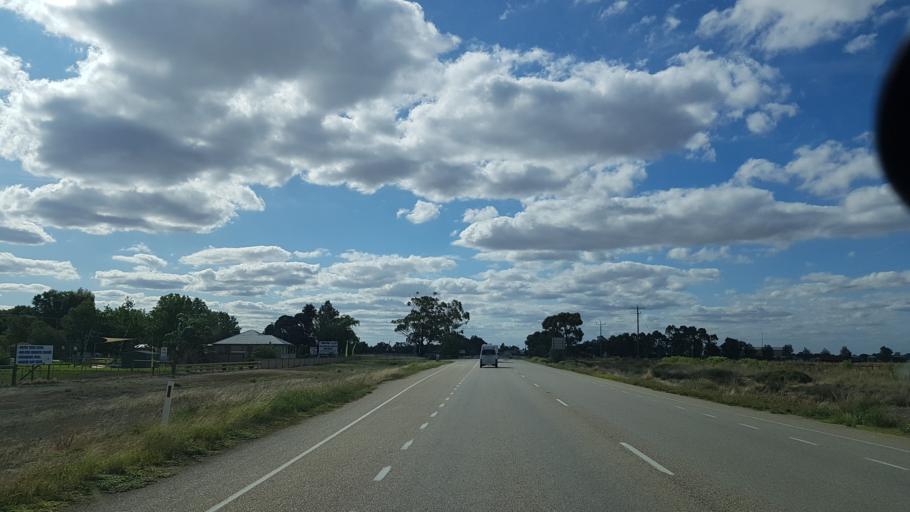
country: AU
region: Victoria
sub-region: Swan Hill
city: Swan Hill
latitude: -35.7613
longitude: 143.9303
